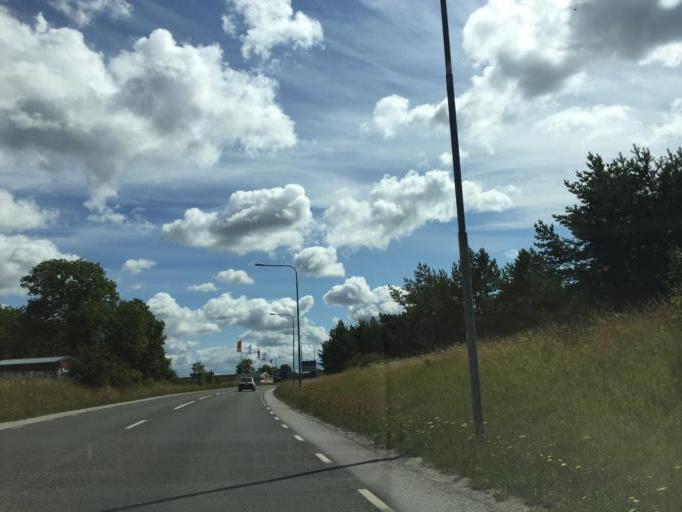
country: SE
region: Gotland
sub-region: Gotland
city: Visby
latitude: 57.6193
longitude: 18.2819
